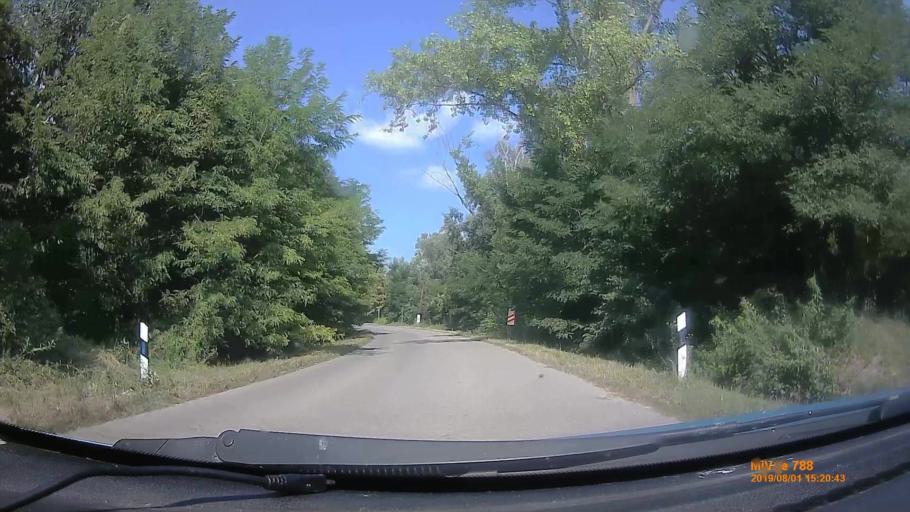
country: HU
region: Baranya
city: Sellye
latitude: 45.8641
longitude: 17.8388
